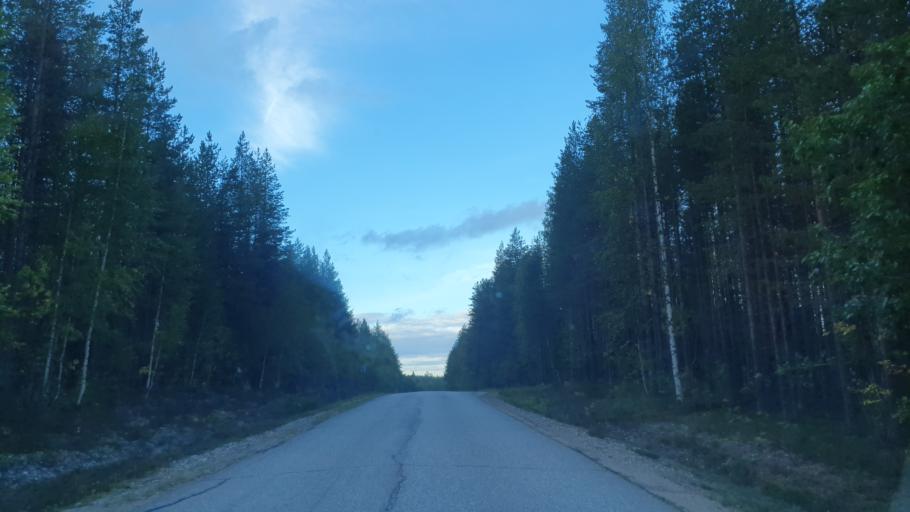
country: FI
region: Kainuu
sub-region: Kehys-Kainuu
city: Kuhmo
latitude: 64.4116
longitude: 29.8838
